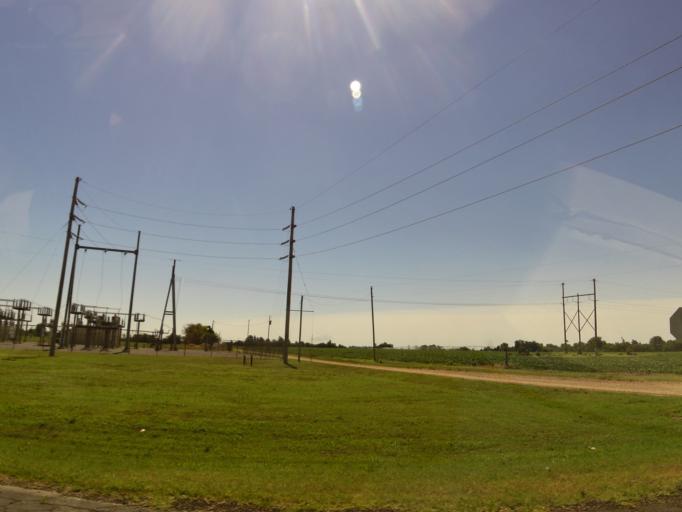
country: US
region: Missouri
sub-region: Dunklin County
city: Malden
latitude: 36.5418
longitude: -89.9627
